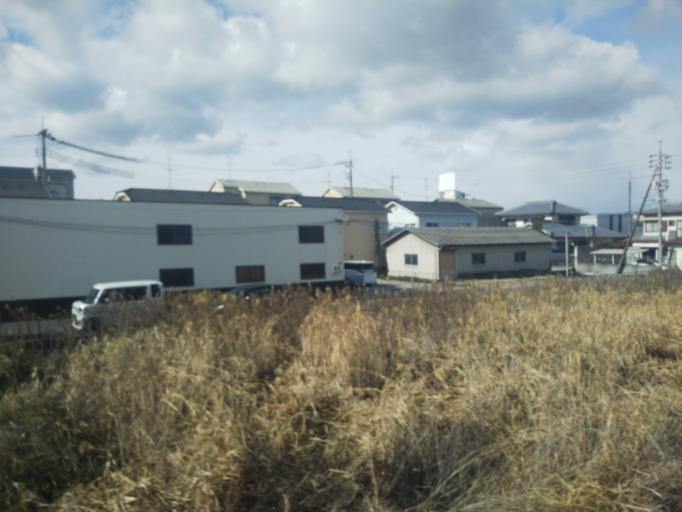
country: JP
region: Okayama
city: Okayama-shi
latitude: 34.6199
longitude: 133.8880
